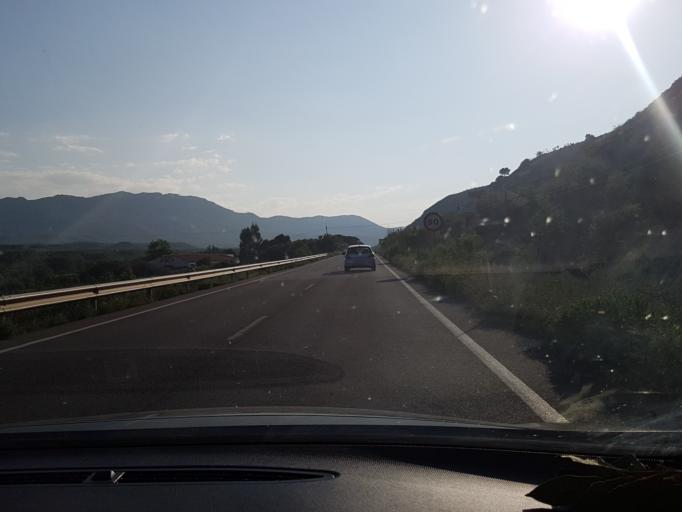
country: ES
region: La Rioja
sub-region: Provincia de La Rioja
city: Herce
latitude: 42.2143
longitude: -2.1322
